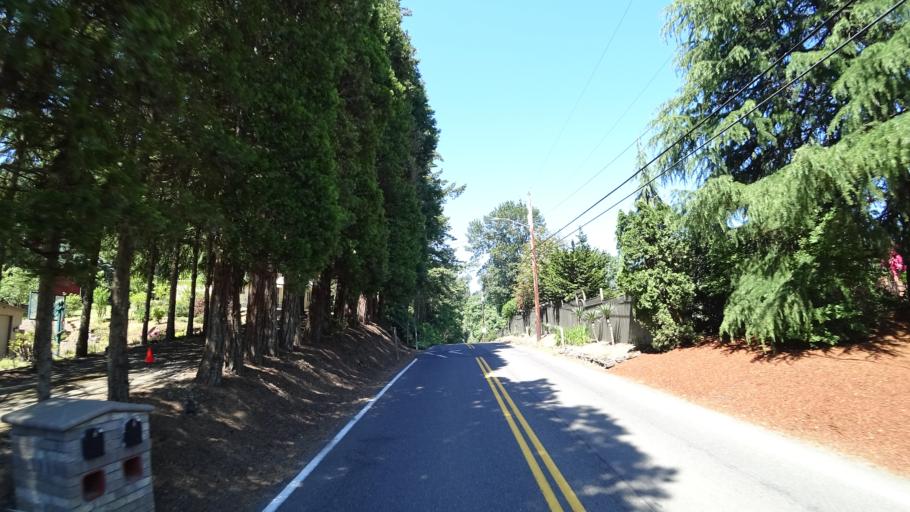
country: US
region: Oregon
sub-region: Clackamas County
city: Happy Valley
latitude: 45.4680
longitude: -122.5317
